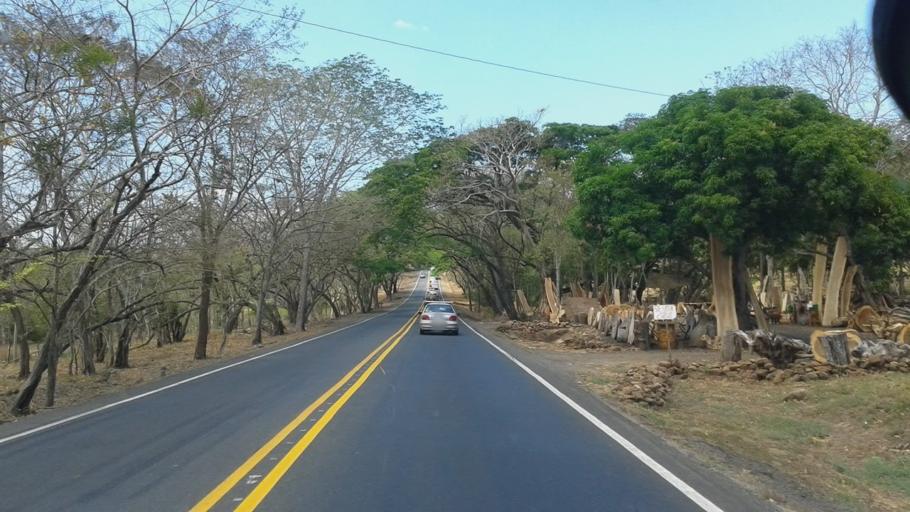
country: CR
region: Guanacaste
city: Juntas
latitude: 10.1463
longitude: -84.9102
